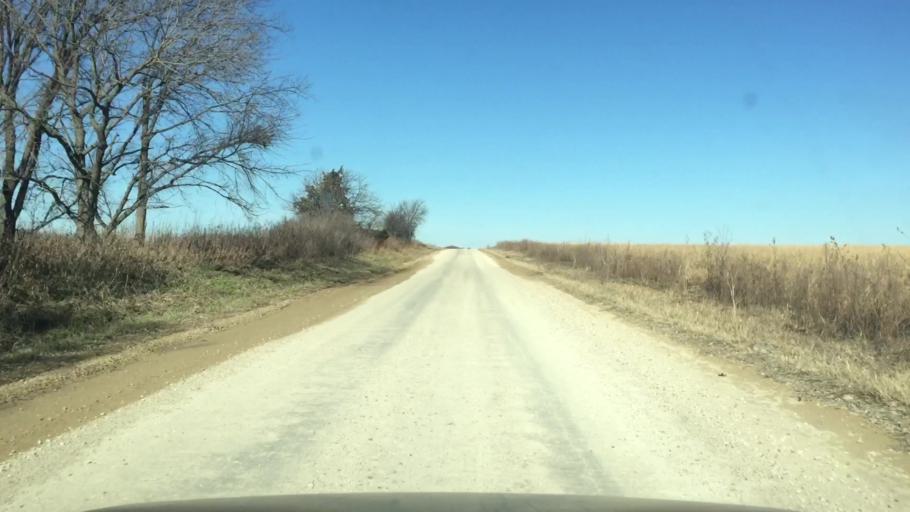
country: US
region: Kansas
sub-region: Allen County
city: Humboldt
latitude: 37.8579
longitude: -95.3910
